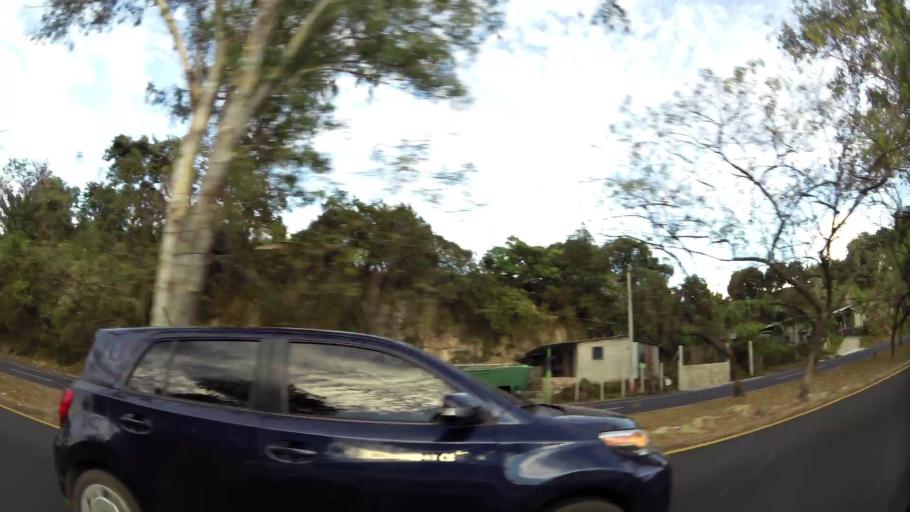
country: SV
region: San Vicente
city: San Sebastian
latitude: 13.6770
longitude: -88.8450
